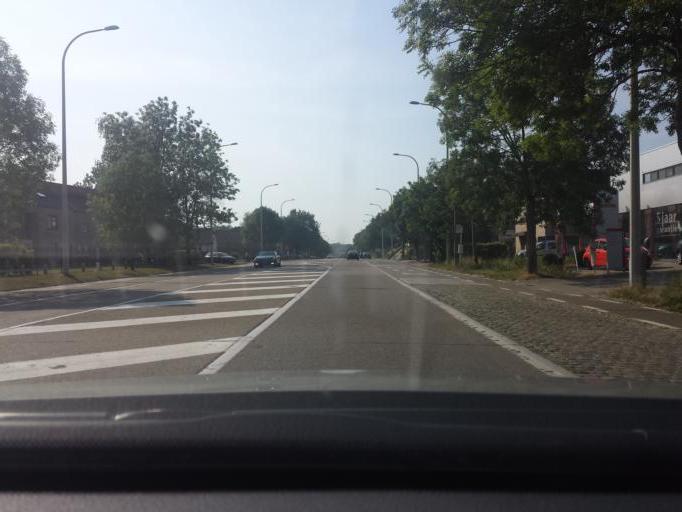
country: BE
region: Flanders
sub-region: Provincie Vlaams-Brabant
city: Diest
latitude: 50.9706
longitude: 5.0726
